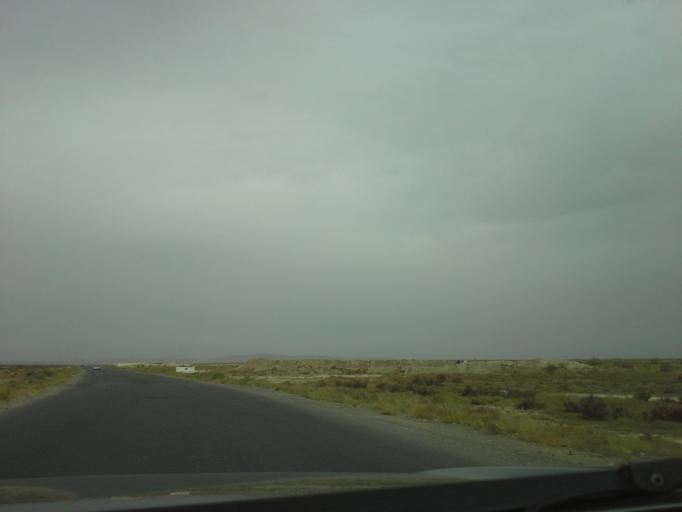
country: TM
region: Lebap
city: Atamyrat
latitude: 37.7296
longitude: 65.5061
